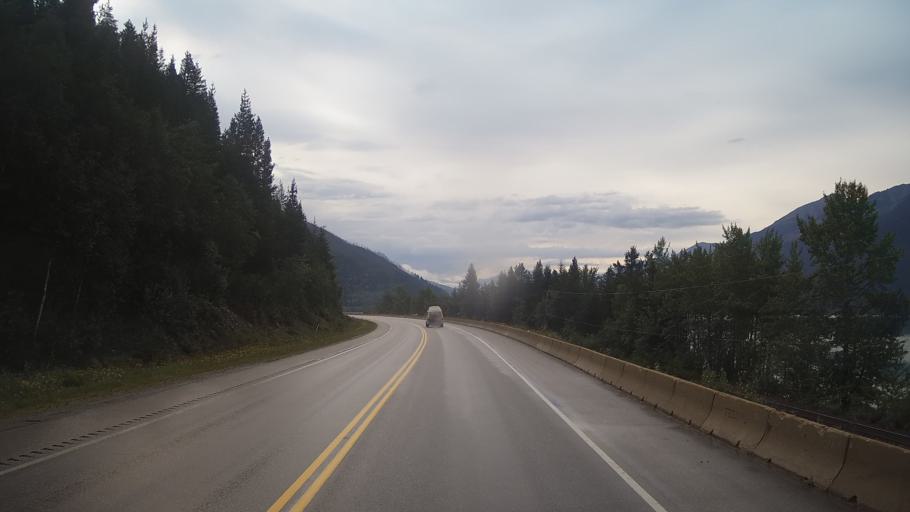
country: CA
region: Alberta
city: Jasper Park Lodge
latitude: 52.9570
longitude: -118.8959
